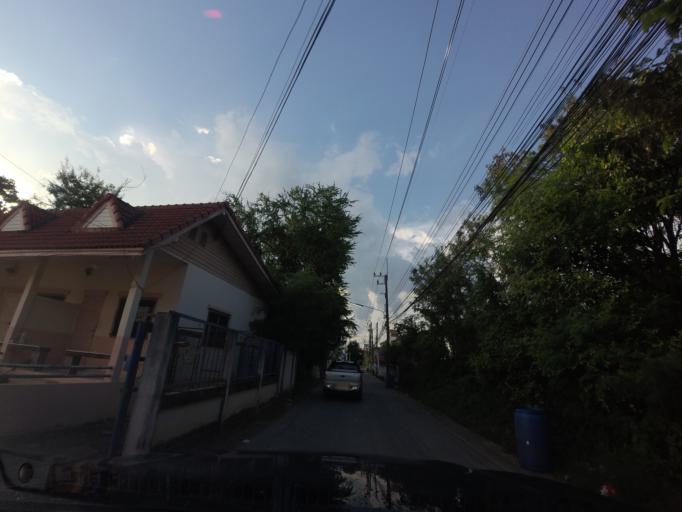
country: TH
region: Khon Kaen
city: Khon Kaen
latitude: 16.4243
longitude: 102.8618
